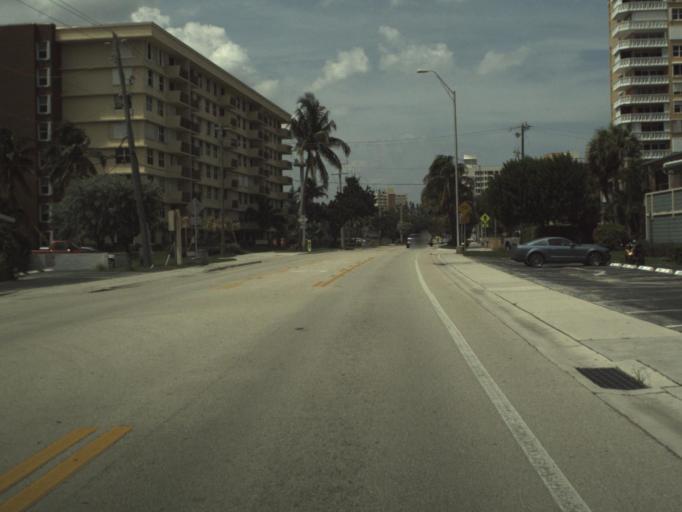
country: US
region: Florida
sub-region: Broward County
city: Lighthouse Point
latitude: 26.2459
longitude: -80.0874
